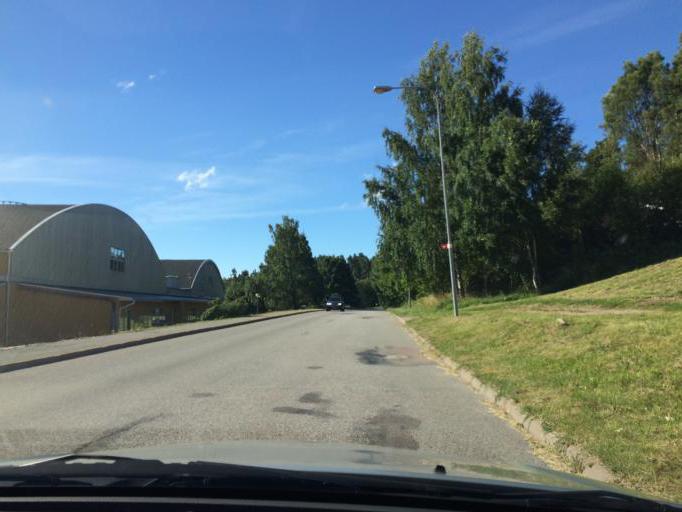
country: SE
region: Vaestmanland
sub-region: Vasteras
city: Vasteras
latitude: 59.5873
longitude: 16.6246
